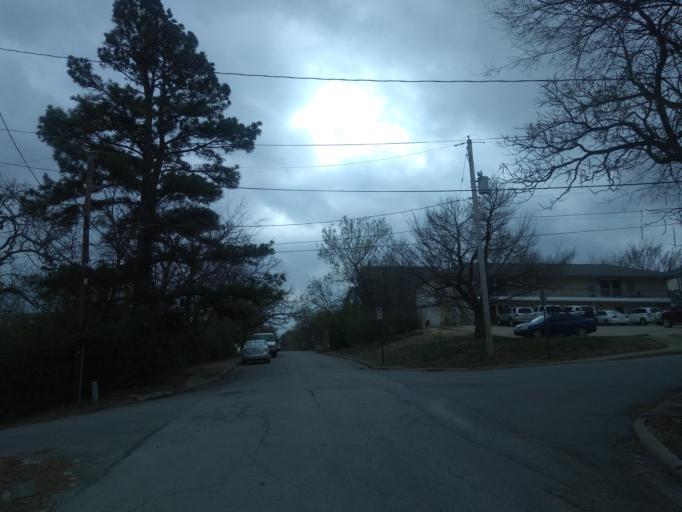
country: US
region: Arkansas
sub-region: Washington County
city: Fayetteville
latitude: 36.0769
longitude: -94.1721
